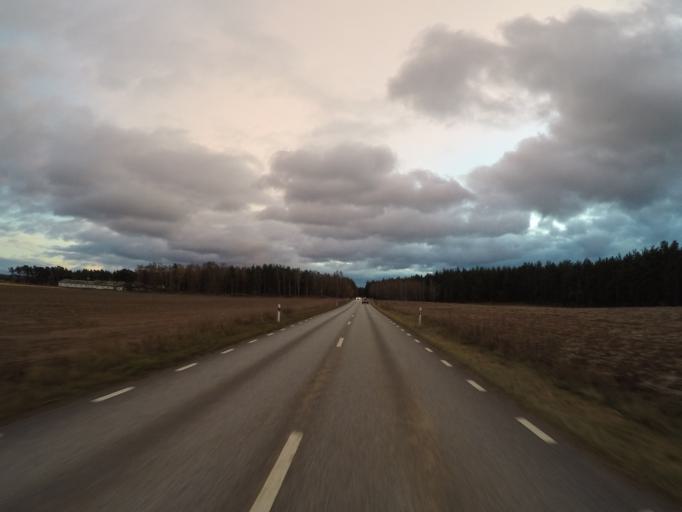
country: SE
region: Skane
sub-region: Kristianstads Kommun
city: Degeberga
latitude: 55.9206
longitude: 14.0735
